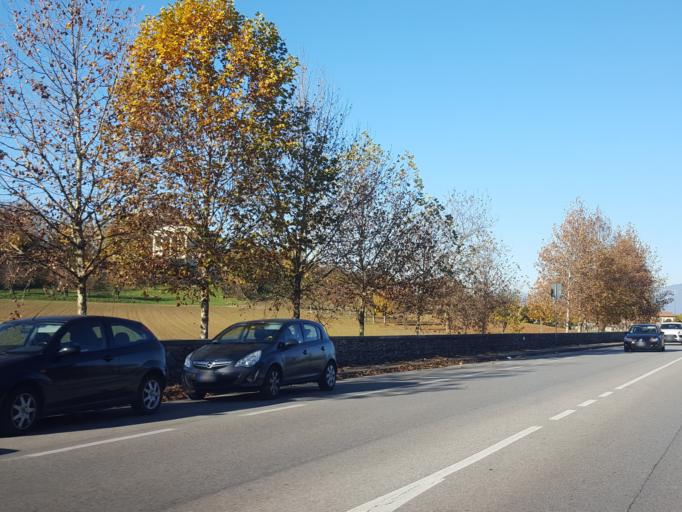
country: IT
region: Veneto
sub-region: Provincia di Vicenza
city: Vicenza
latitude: 45.5296
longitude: 11.5630
